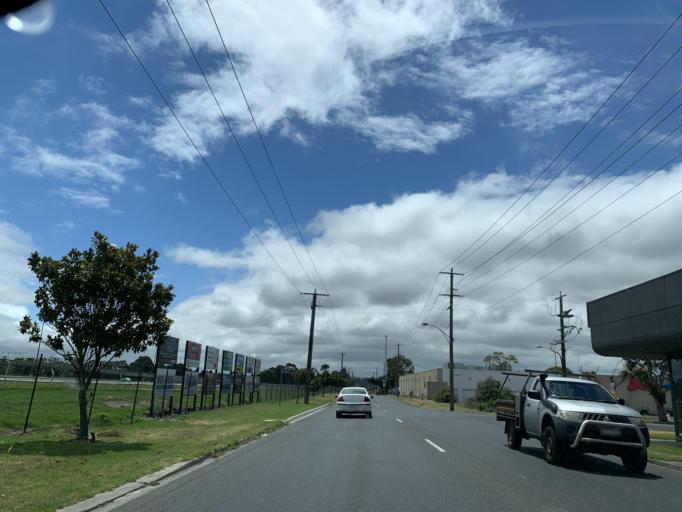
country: AU
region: Victoria
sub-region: Latrobe
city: Moe
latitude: -38.1751
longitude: 146.2574
